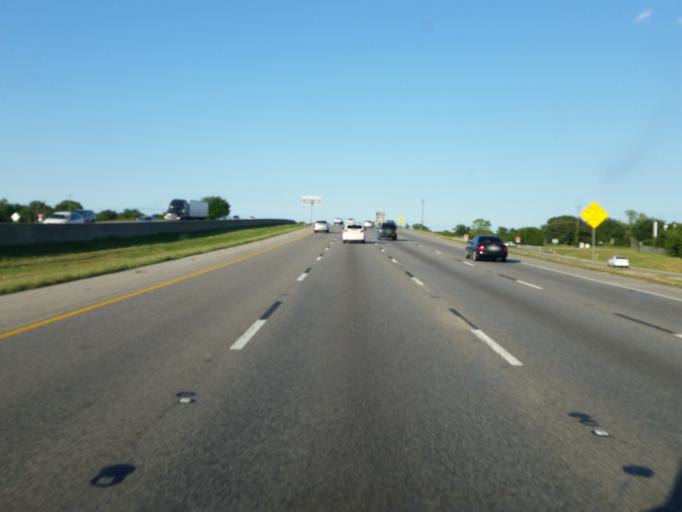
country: US
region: Texas
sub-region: Dallas County
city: Balch Springs
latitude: 32.6821
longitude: -96.6601
